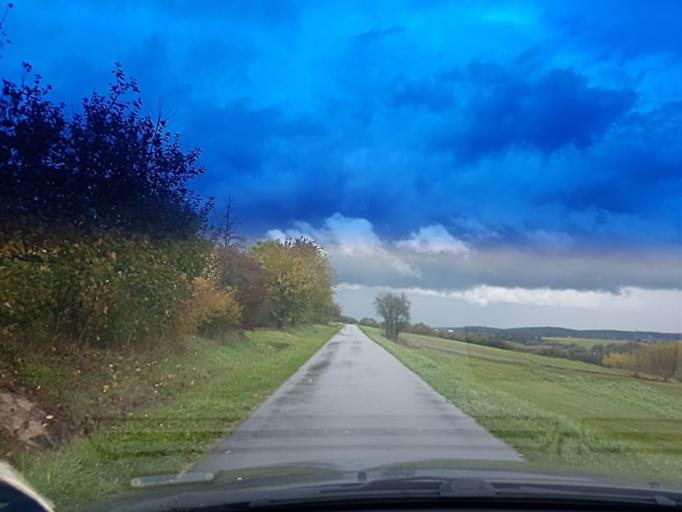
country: DE
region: Bavaria
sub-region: Regierungsbezirk Mittelfranken
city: Burghaslach
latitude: 49.7348
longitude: 10.6080
